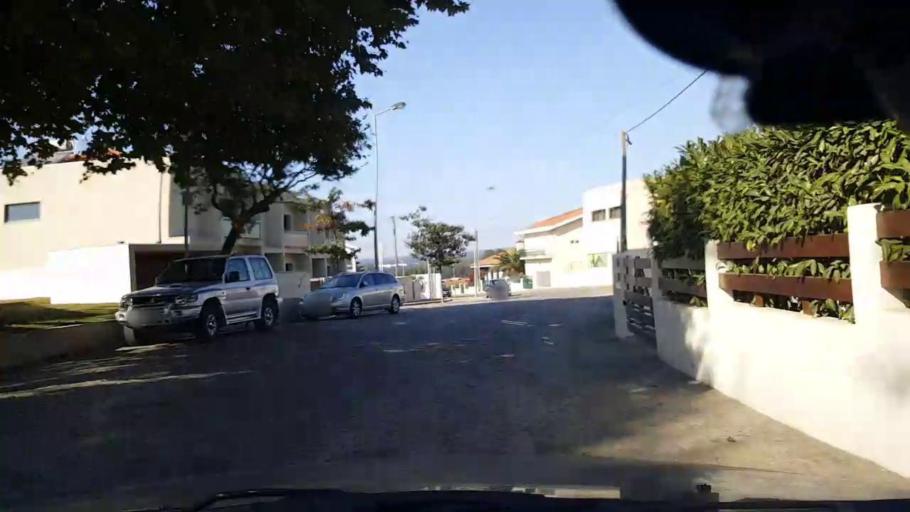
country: PT
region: Porto
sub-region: Vila do Conde
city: Arvore
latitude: 41.3508
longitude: -8.7181
